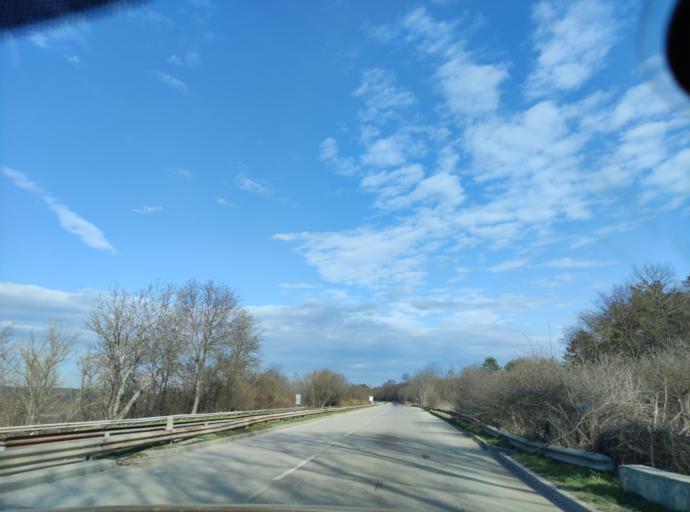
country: BG
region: Pleven
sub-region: Obshtina Dolna Mitropoliya
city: Dolna Mitropoliya
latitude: 43.4331
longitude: 24.5508
